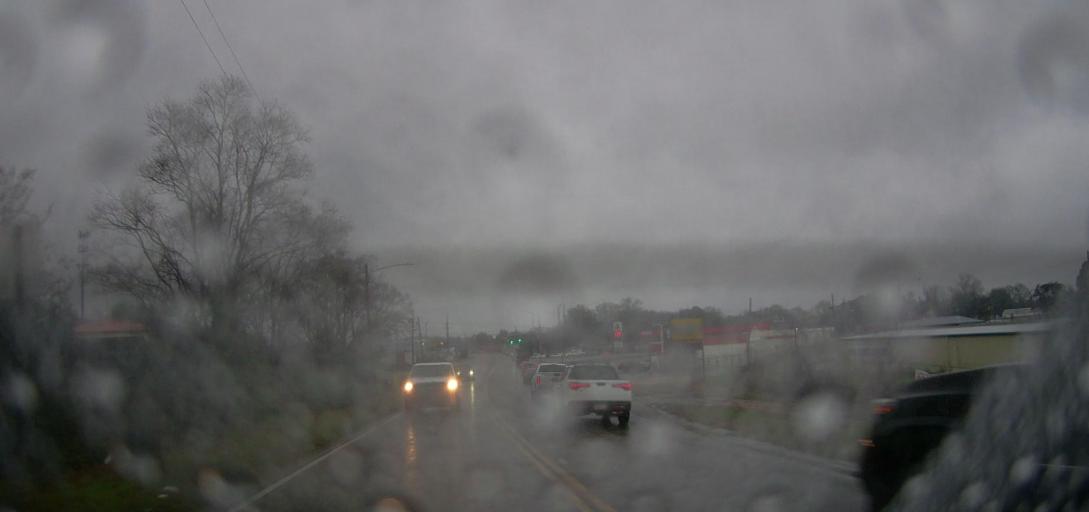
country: US
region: Alabama
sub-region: Montgomery County
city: Montgomery
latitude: 32.3699
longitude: -86.3508
